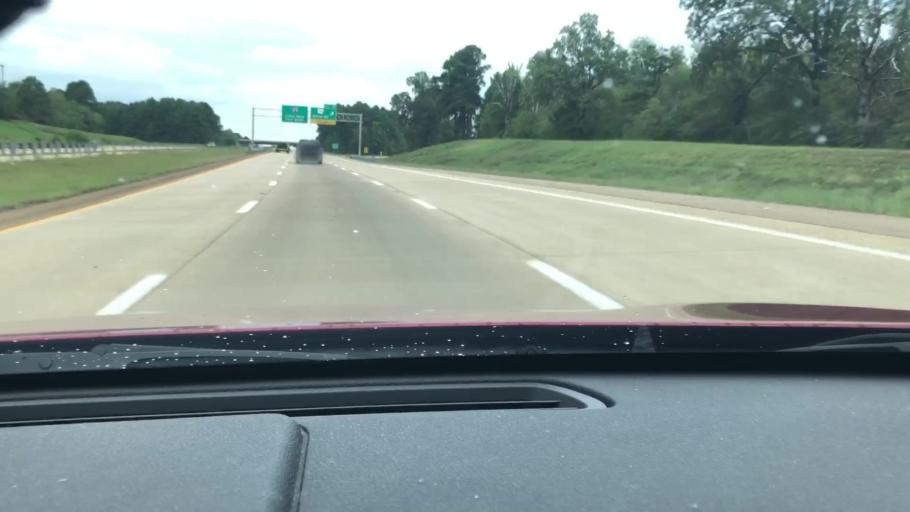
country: US
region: Texas
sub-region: Bowie County
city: Texarkana
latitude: 33.4056
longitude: -94.0047
